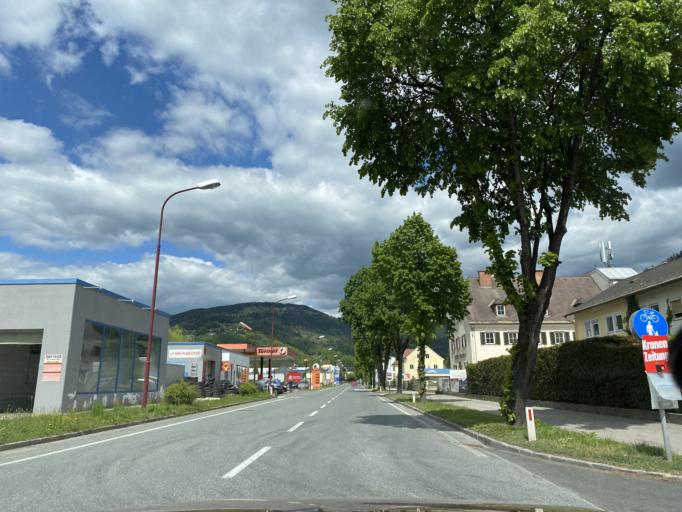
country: AT
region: Carinthia
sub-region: Politischer Bezirk Wolfsberg
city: Wolfsberg
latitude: 46.8454
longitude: 14.8434
